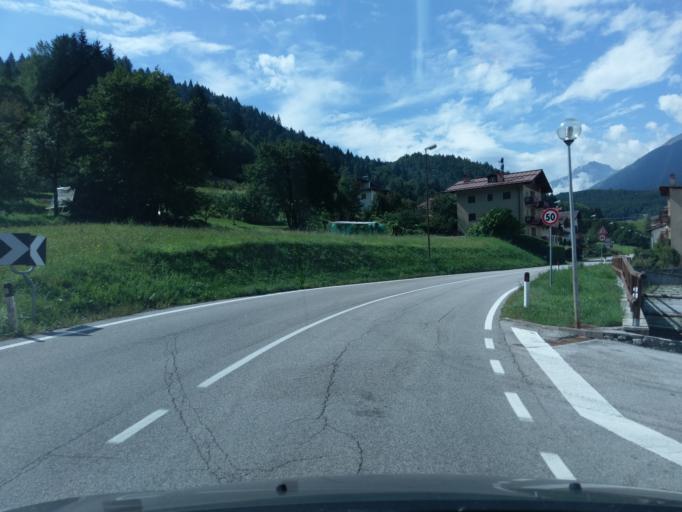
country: IT
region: Trentino-Alto Adige
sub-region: Provincia di Trento
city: Cavedago
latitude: 46.1860
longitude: 11.0405
